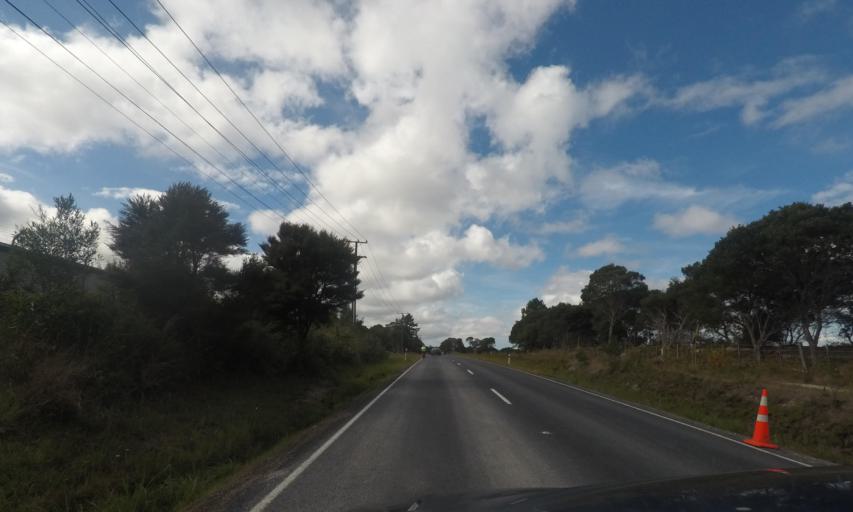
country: NZ
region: Auckland
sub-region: Auckland
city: Rosebank
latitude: -36.7897
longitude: 174.6377
